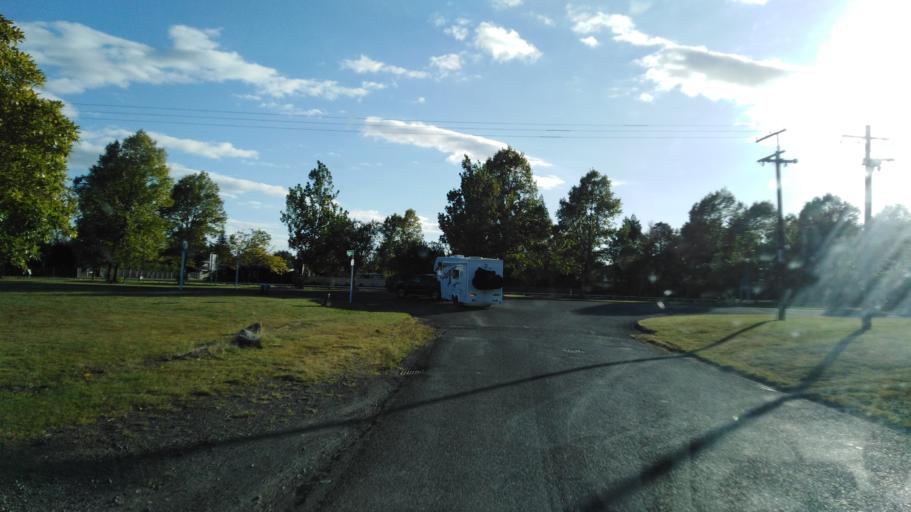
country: NZ
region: Waikato
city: Turangi
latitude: -38.9951
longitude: 175.7998
